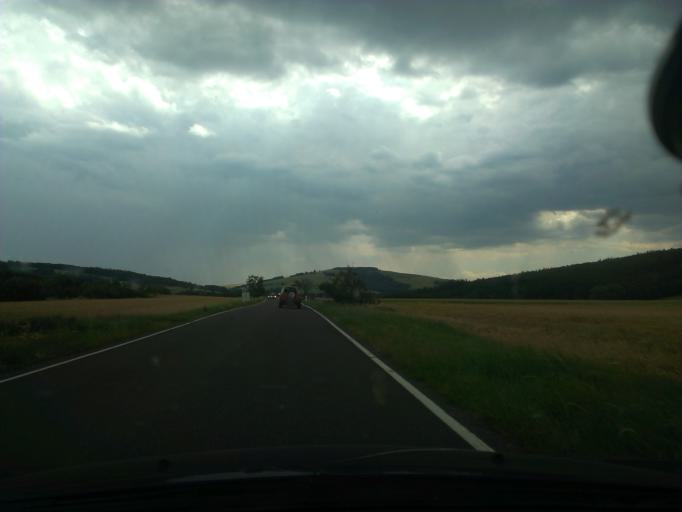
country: CZ
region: South Moravian
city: Velka nad Velickou
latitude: 48.8394
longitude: 17.5194
